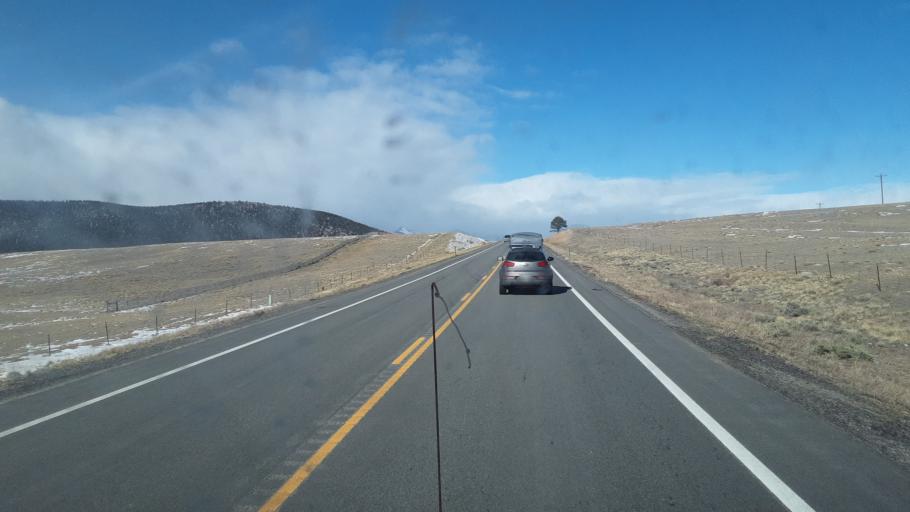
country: US
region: Colorado
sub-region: Park County
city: Fairplay
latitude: 39.0863
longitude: -105.9798
